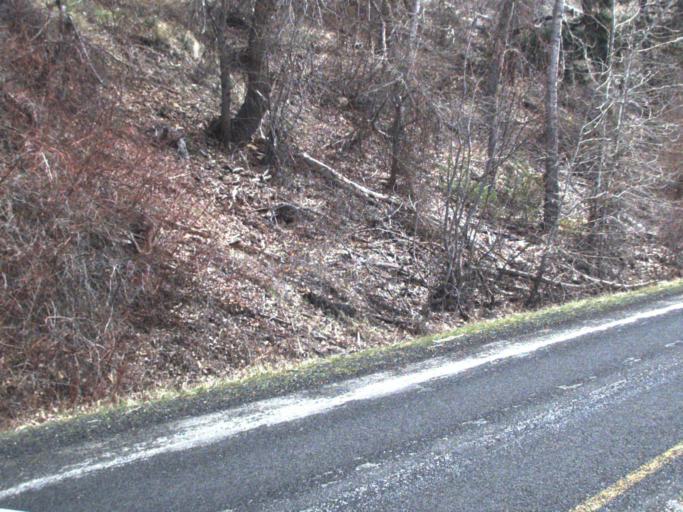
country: US
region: Washington
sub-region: Yakima County
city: Tieton
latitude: 46.8597
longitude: -120.9531
